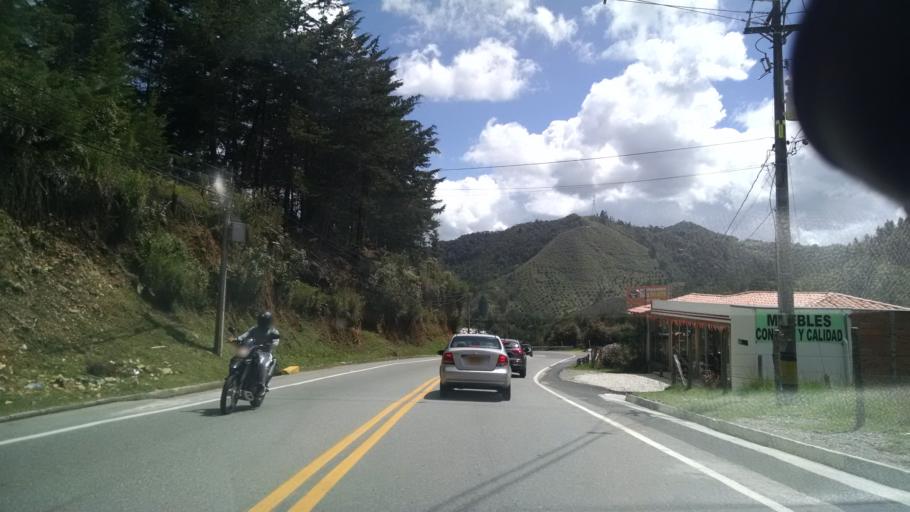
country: CO
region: Antioquia
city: El Retiro
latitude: 6.1364
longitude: -75.5100
